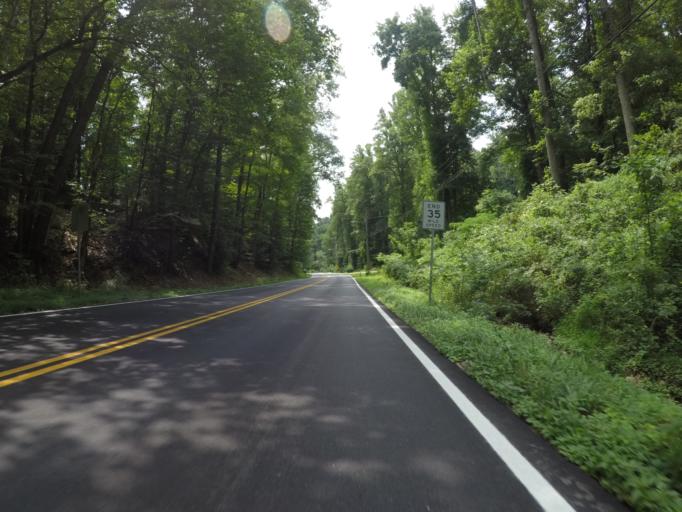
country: US
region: Kentucky
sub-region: Boyd County
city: Ashland
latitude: 38.4462
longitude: -82.6369
